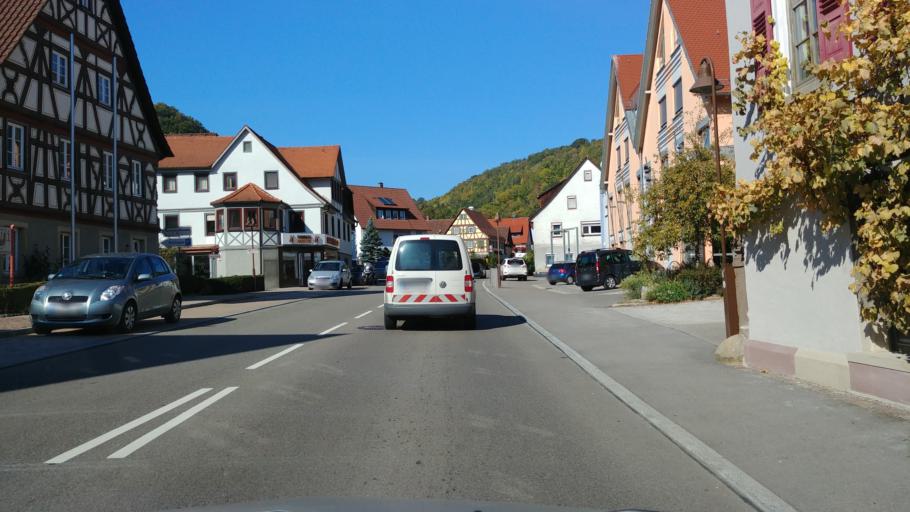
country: DE
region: Baden-Wuerttemberg
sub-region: Regierungsbezirk Stuttgart
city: Untermunkheim
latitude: 49.1532
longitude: 9.7332
